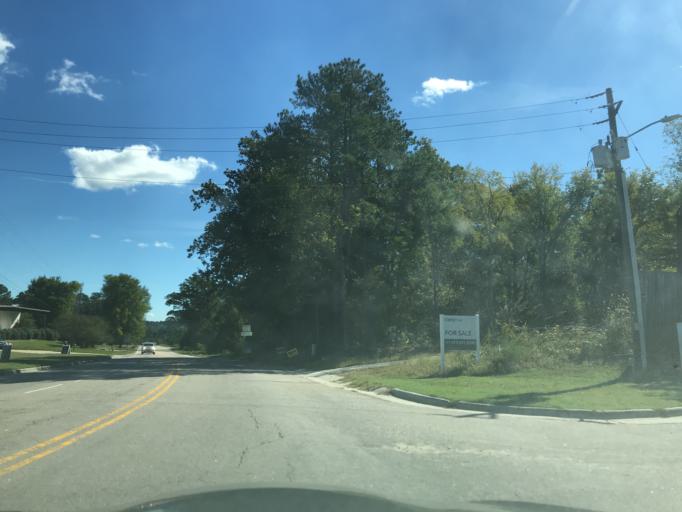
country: US
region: North Carolina
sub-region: Wake County
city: Wake Forest
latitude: 35.9183
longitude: -78.5461
